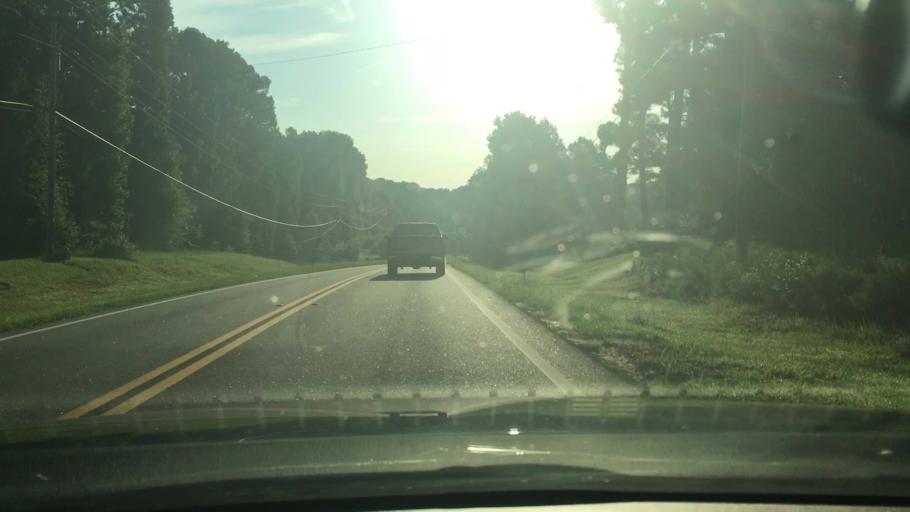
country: US
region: Georgia
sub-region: Fayette County
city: Peachtree City
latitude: 33.3863
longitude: -84.6514
